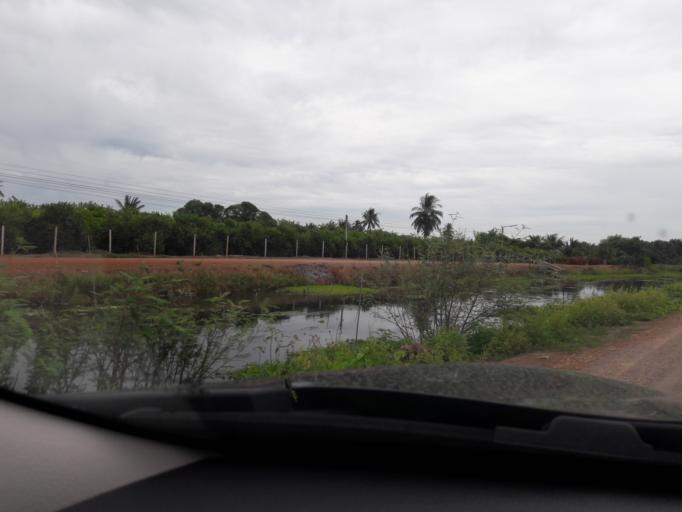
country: TH
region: Ratchaburi
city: Bang Phae
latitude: 13.6206
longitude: 99.9623
